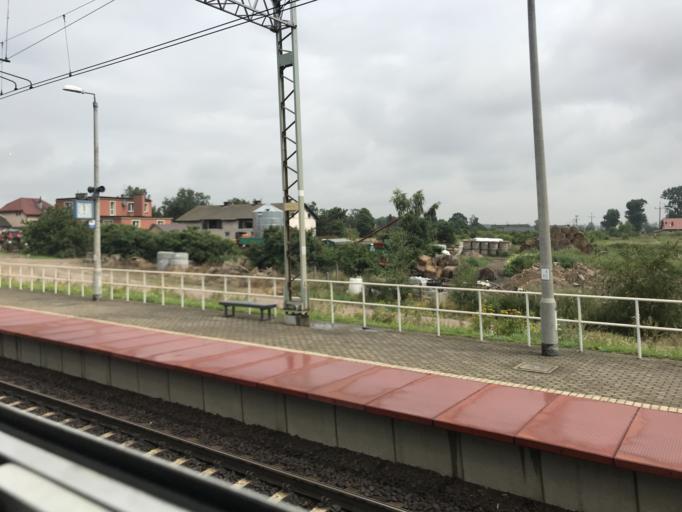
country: PL
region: Pomeranian Voivodeship
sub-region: Powiat gdanski
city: Legowo
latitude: 54.2321
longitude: 18.6477
